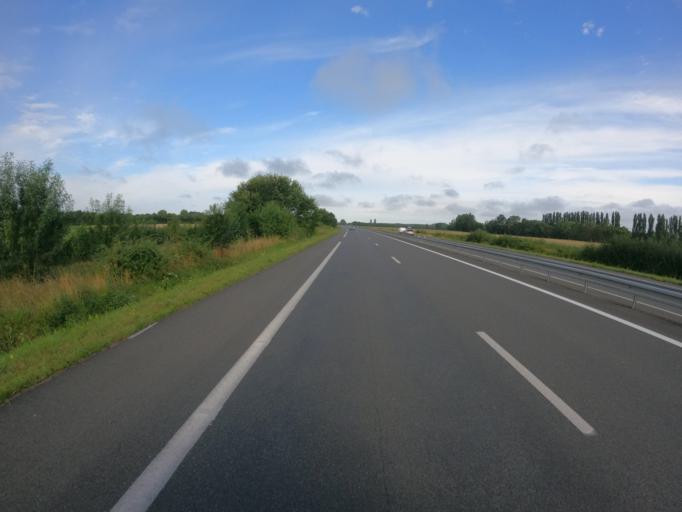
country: FR
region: Pays de la Loire
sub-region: Departement de Maine-et-Loire
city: Allonnes
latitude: 47.2859
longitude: 0.0091
